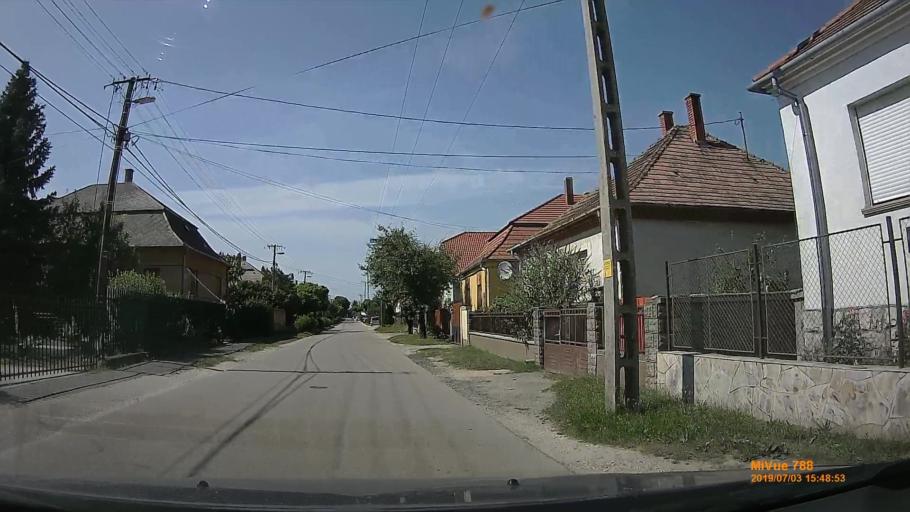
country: HU
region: Gyor-Moson-Sopron
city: Toltestava
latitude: 47.6948
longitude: 17.7356
